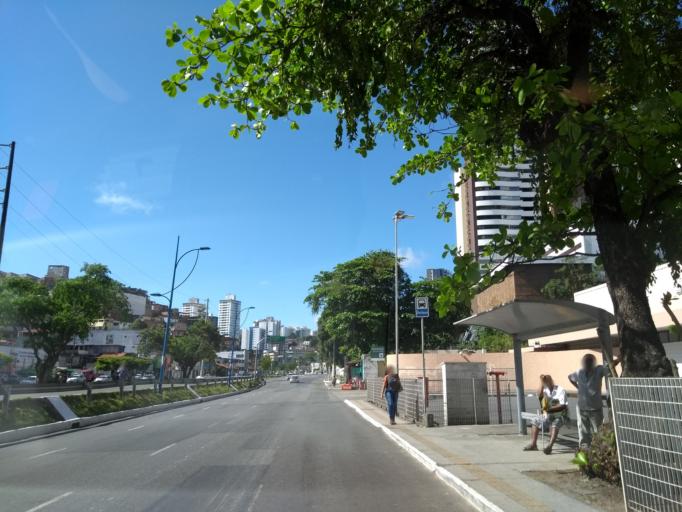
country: BR
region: Bahia
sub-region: Salvador
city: Salvador
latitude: -13.0023
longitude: -38.4920
